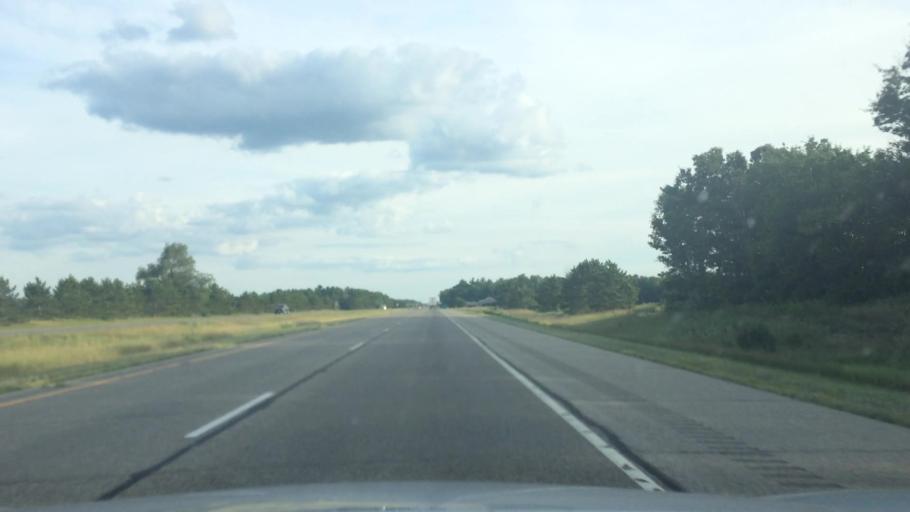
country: US
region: Wisconsin
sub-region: Portage County
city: Plover
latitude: 44.2716
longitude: -89.5239
